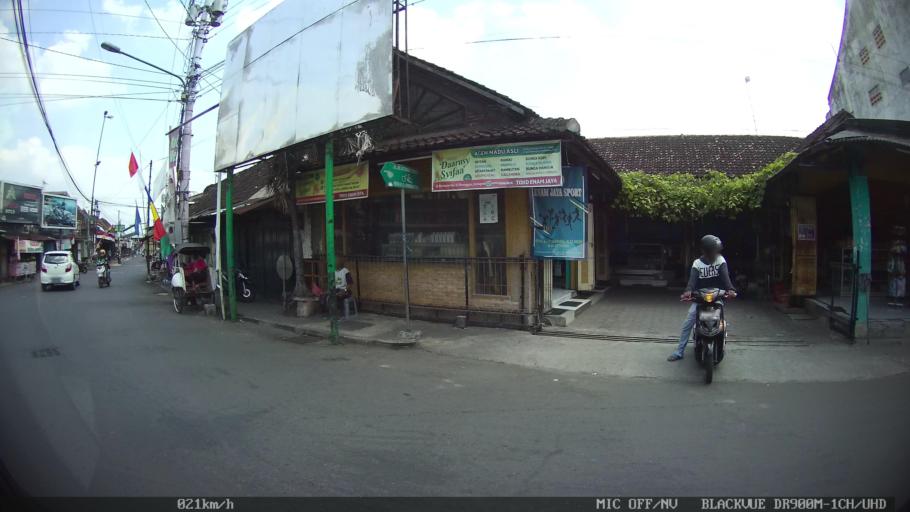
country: ID
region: Daerah Istimewa Yogyakarta
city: Yogyakarta
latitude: -7.8282
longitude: 110.4008
